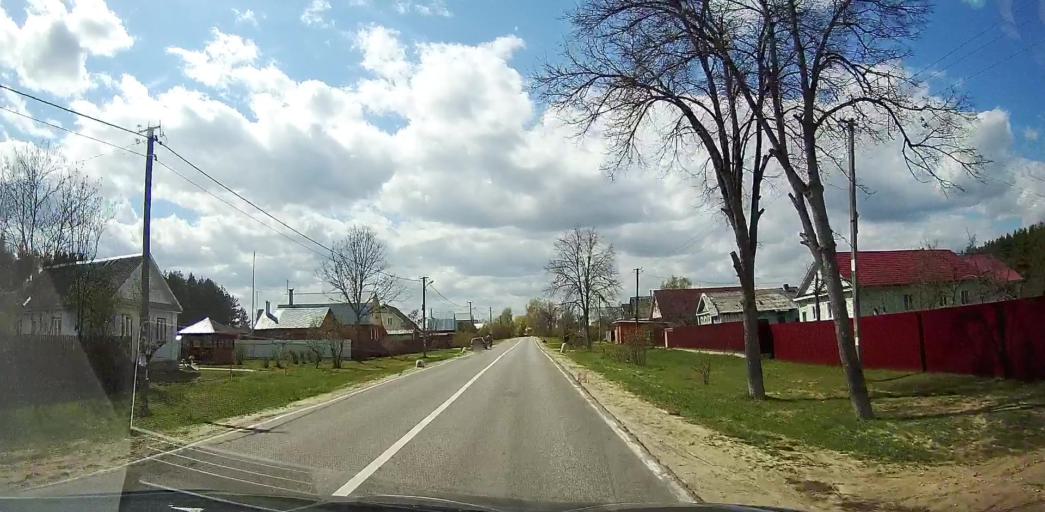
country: RU
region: Moskovskaya
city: Davydovo
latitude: 55.5570
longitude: 38.8270
